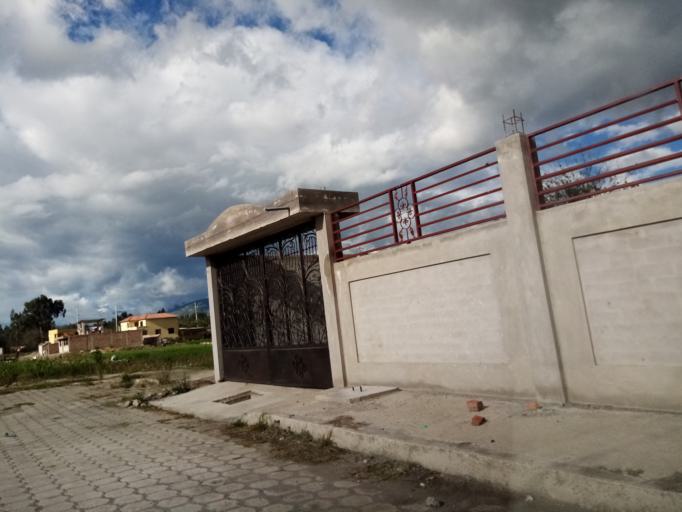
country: EC
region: Chimborazo
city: Riobamba
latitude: -1.6866
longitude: -78.6259
